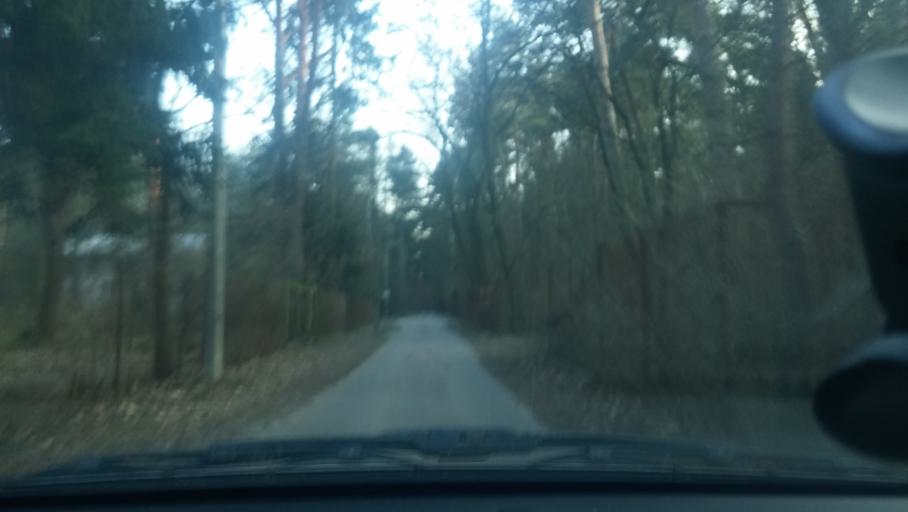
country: PL
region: Masovian Voivodeship
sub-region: Warszawa
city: Wawer
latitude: 52.2080
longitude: 21.2039
